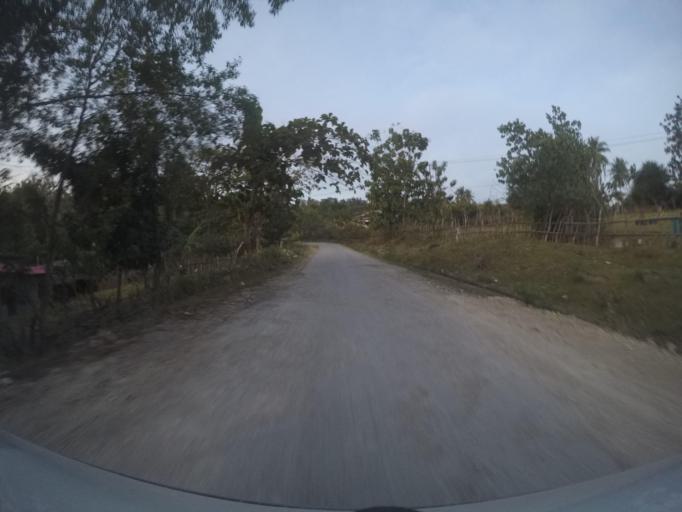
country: TL
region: Viqueque
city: Viqueque
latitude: -8.8865
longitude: 126.3863
